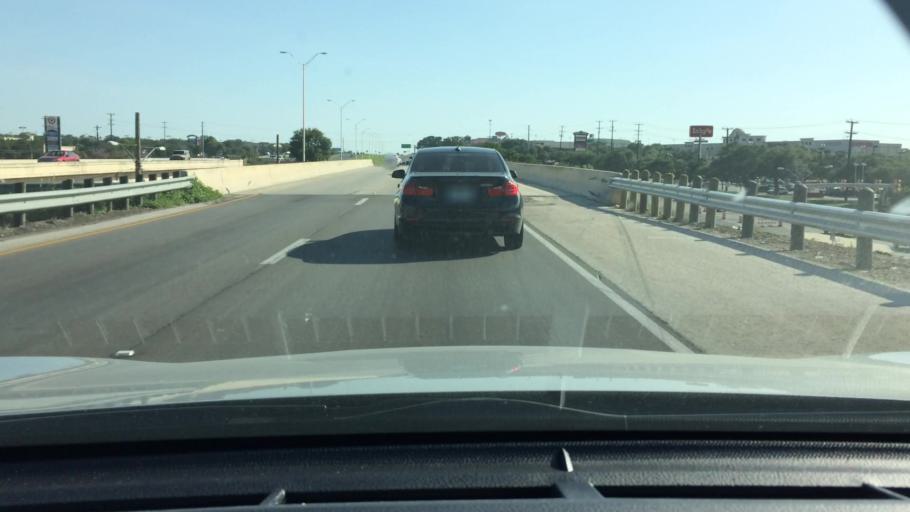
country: US
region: Texas
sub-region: Bexar County
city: Helotes
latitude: 29.5542
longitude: -98.6669
